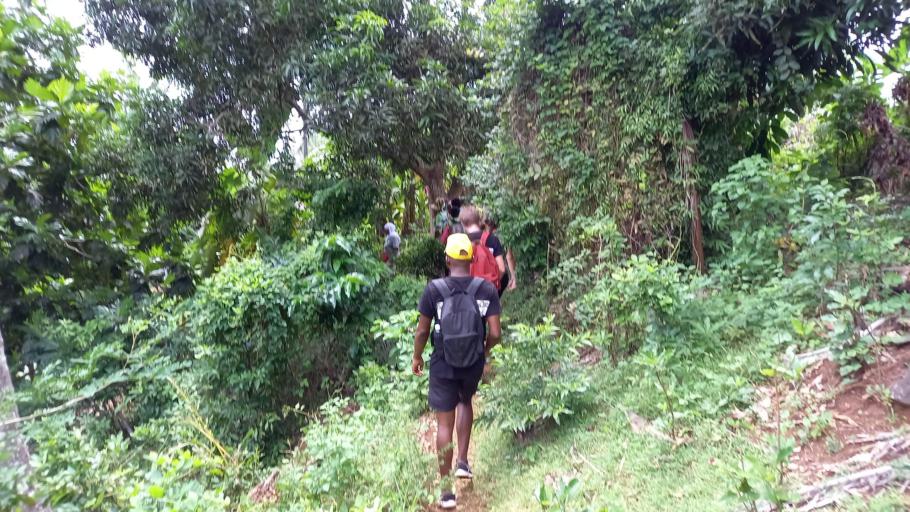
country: YT
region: Acoua
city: Acoua
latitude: -12.7111
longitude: 45.0558
